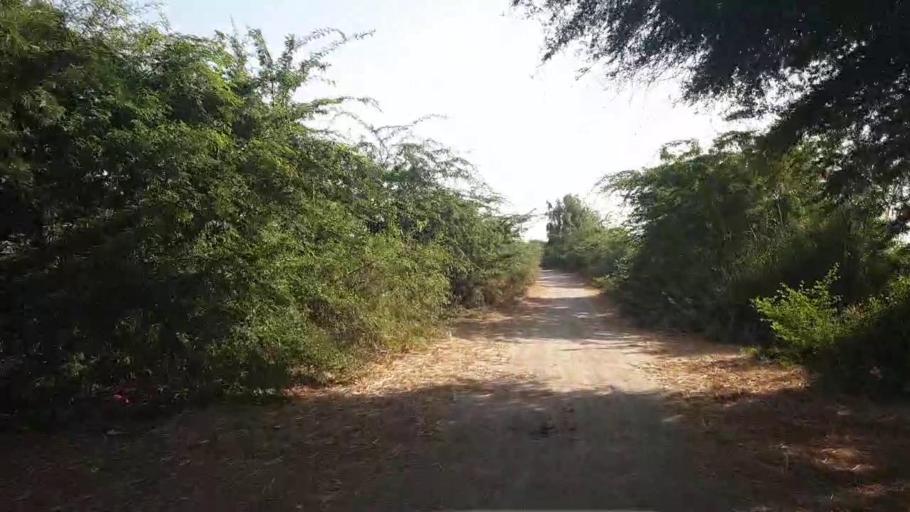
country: PK
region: Sindh
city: Matli
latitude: 25.0094
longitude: 68.7406
